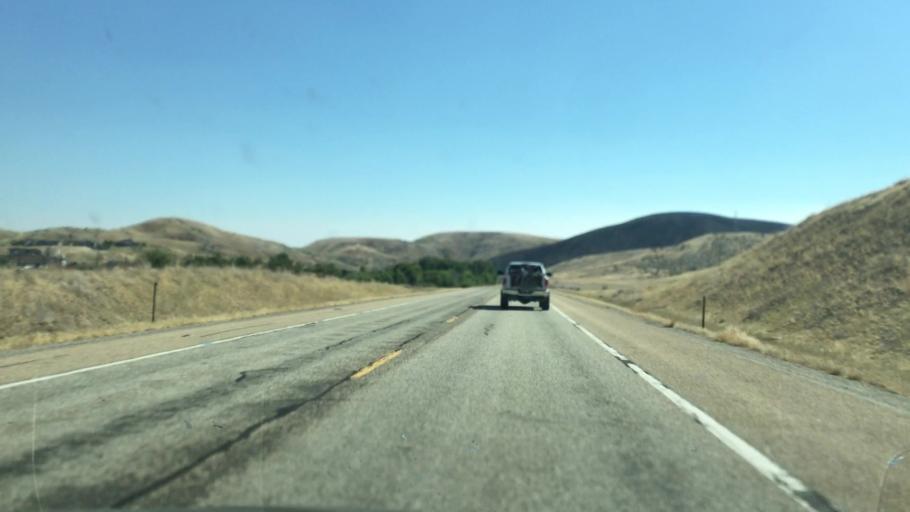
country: US
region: Idaho
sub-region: Ada County
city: Eagle
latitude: 43.7798
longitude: -116.2641
